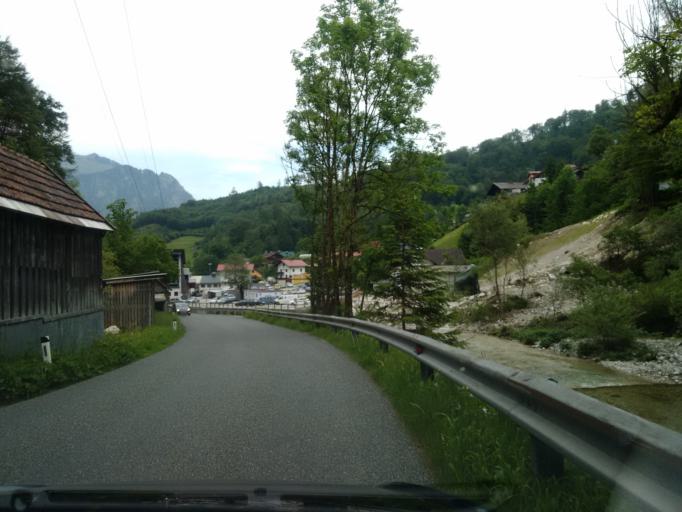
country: AT
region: Upper Austria
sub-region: Politischer Bezirk Gmunden
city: Ebensee
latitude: 47.8130
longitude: 13.7559
